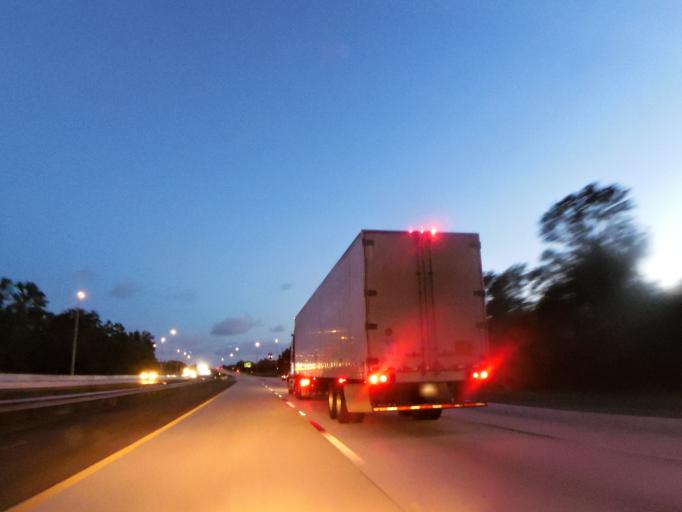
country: US
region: Florida
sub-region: Duval County
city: Jacksonville
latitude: 30.4378
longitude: -81.6537
